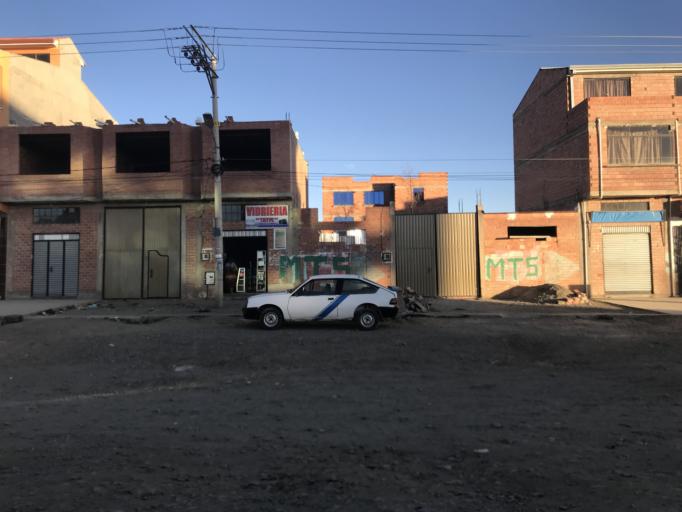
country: BO
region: La Paz
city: La Paz
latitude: -16.5042
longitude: -68.2489
